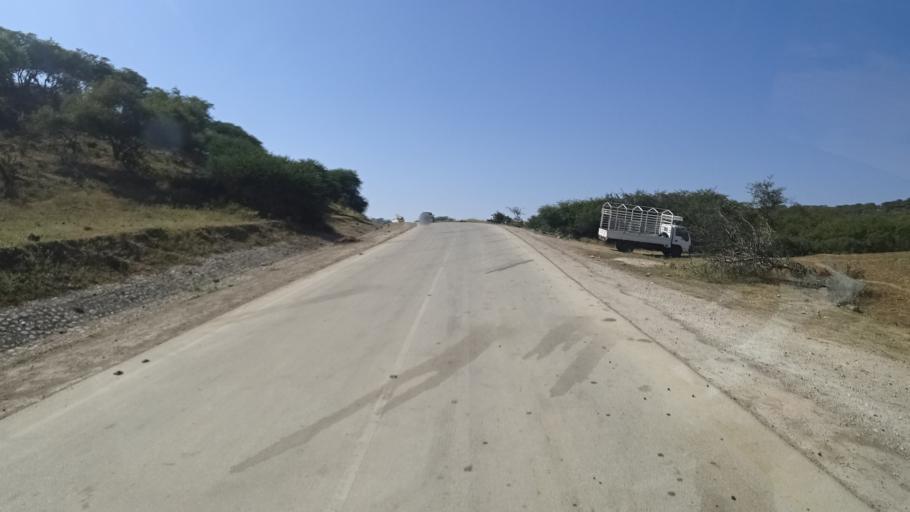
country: OM
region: Zufar
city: Salalah
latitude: 17.0654
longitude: 54.6022
